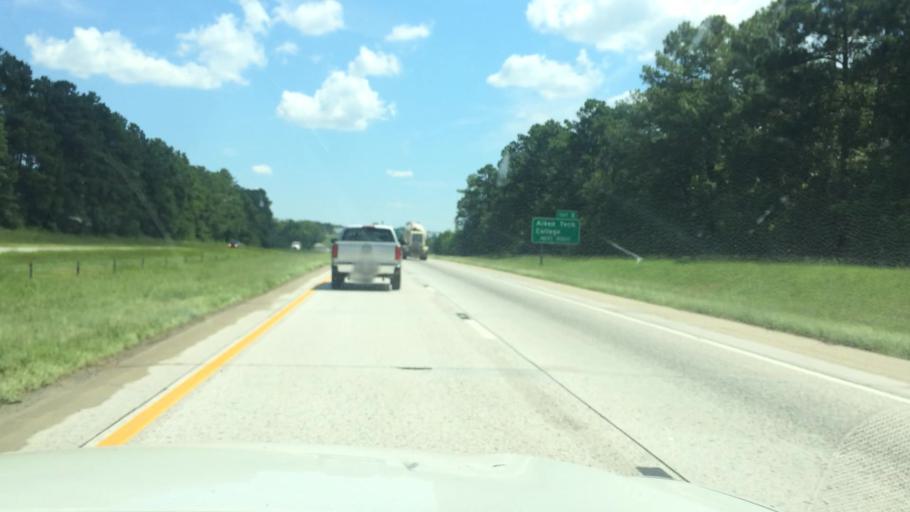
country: US
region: South Carolina
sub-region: Aiken County
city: Belvedere
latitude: 33.5587
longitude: -81.9441
